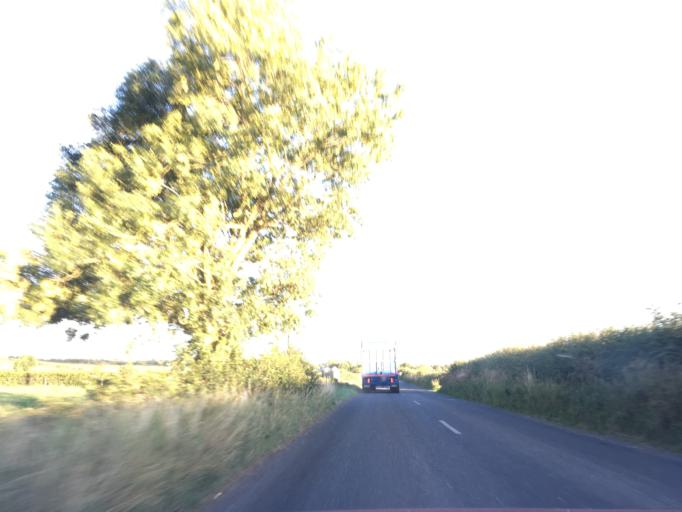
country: IE
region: Munster
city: Cashel
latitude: 52.4700
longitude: -7.9217
